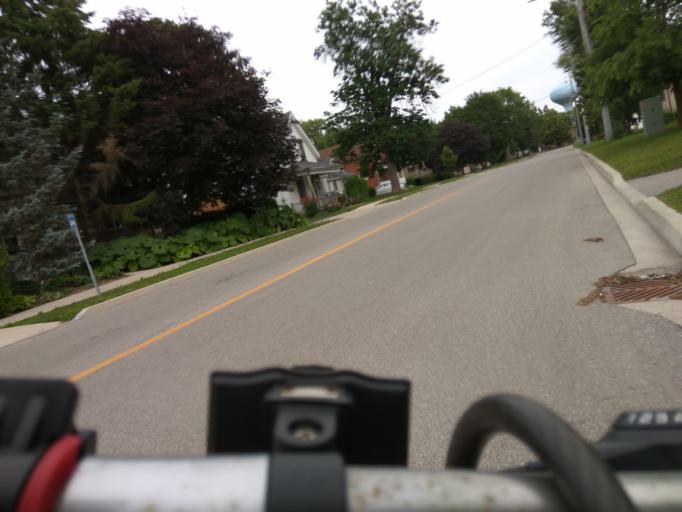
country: CA
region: Ontario
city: Stratford
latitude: 43.3597
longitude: -80.9925
